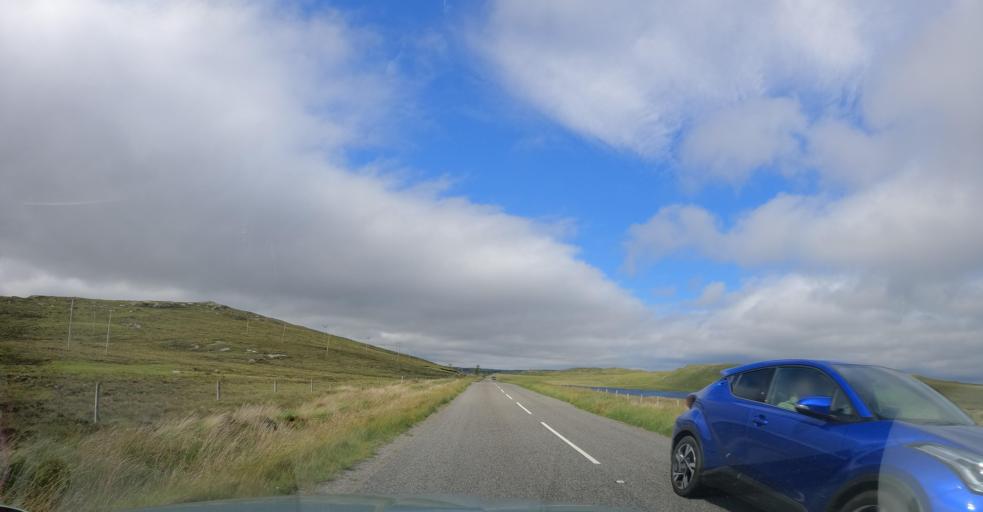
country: GB
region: Scotland
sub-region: Eilean Siar
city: Stornoway
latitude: 58.1263
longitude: -6.5073
